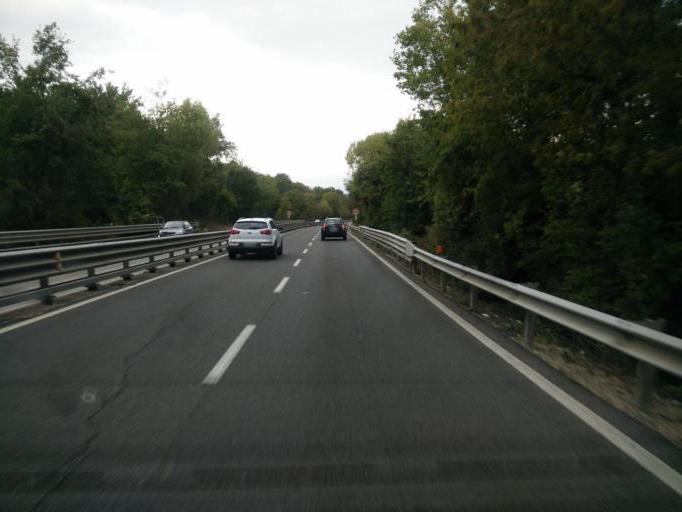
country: IT
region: Tuscany
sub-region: Province of Florence
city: Sambuca
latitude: 43.5748
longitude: 11.2058
